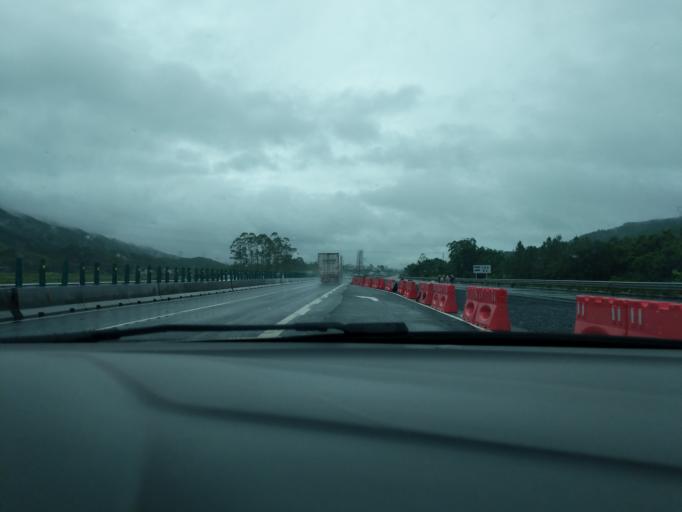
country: CN
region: Guangdong
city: Pingshi
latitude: 22.2483
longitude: 112.3057
